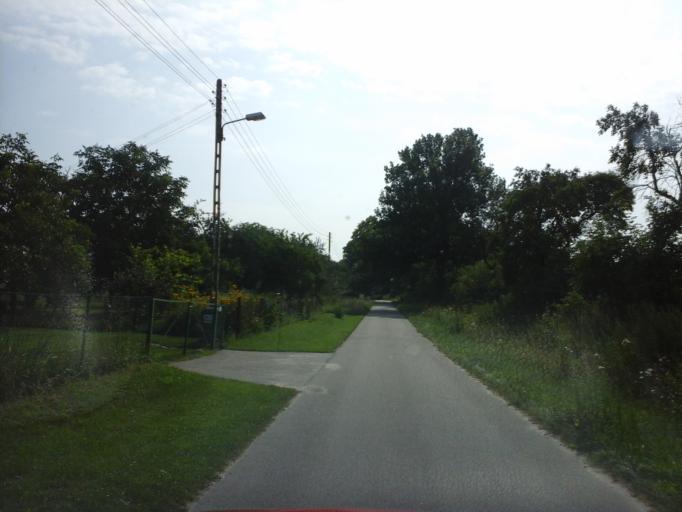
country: PL
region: West Pomeranian Voivodeship
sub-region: Powiat mysliborski
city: Barlinek
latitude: 53.0462
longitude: 15.2357
